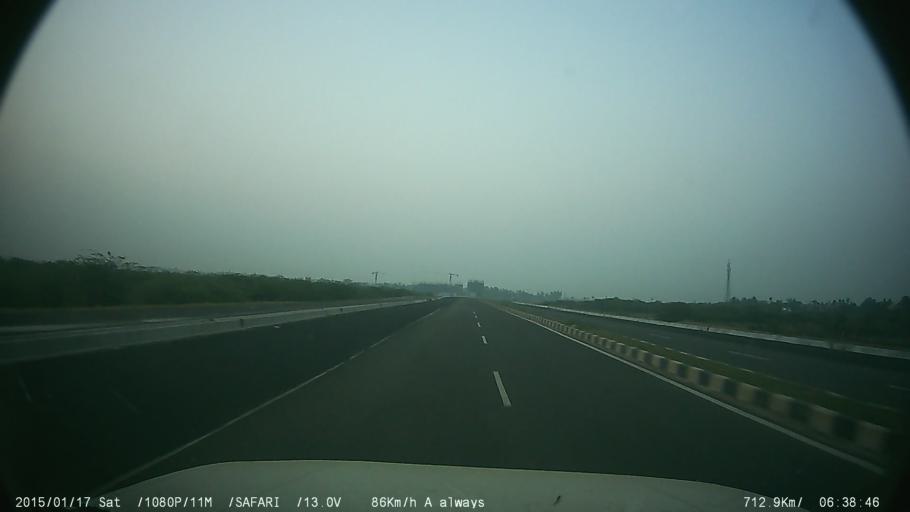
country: IN
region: Tamil Nadu
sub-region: Kancheepuram
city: Sriperumbudur
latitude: 12.9315
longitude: 79.9346
